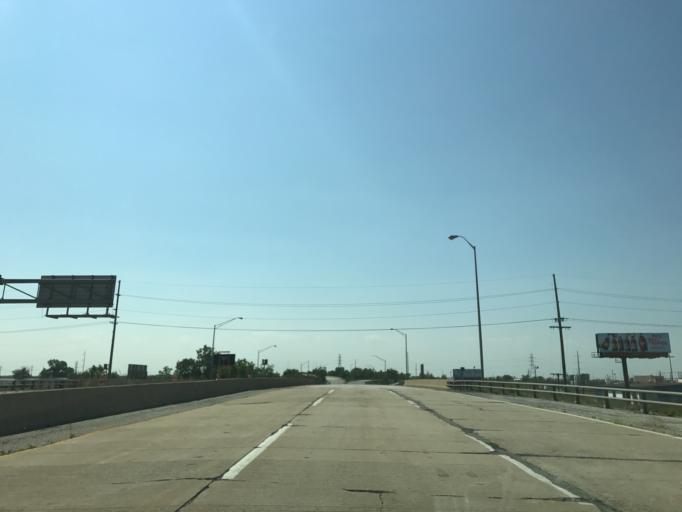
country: US
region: Indiana
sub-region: Lake County
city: Whiting
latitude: 41.6571
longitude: -87.5072
